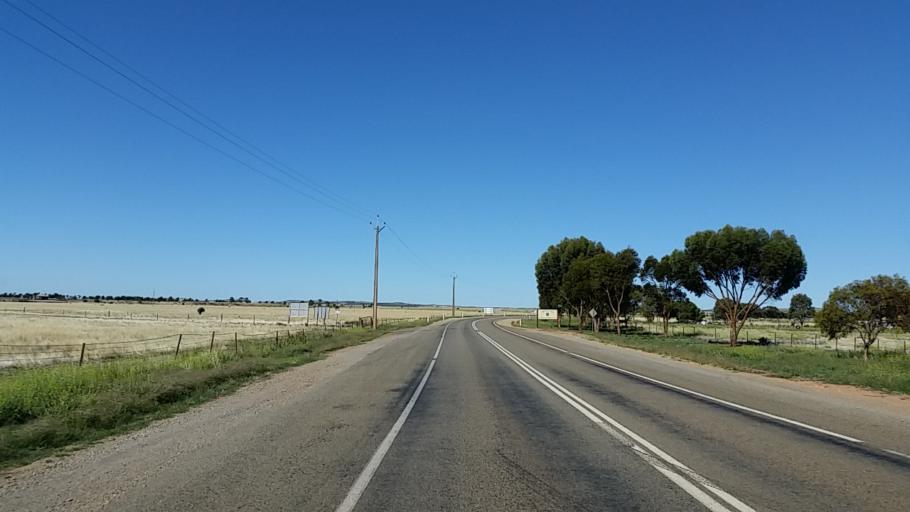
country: AU
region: South Australia
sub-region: Peterborough
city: Peterborough
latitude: -32.9716
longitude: 138.8497
